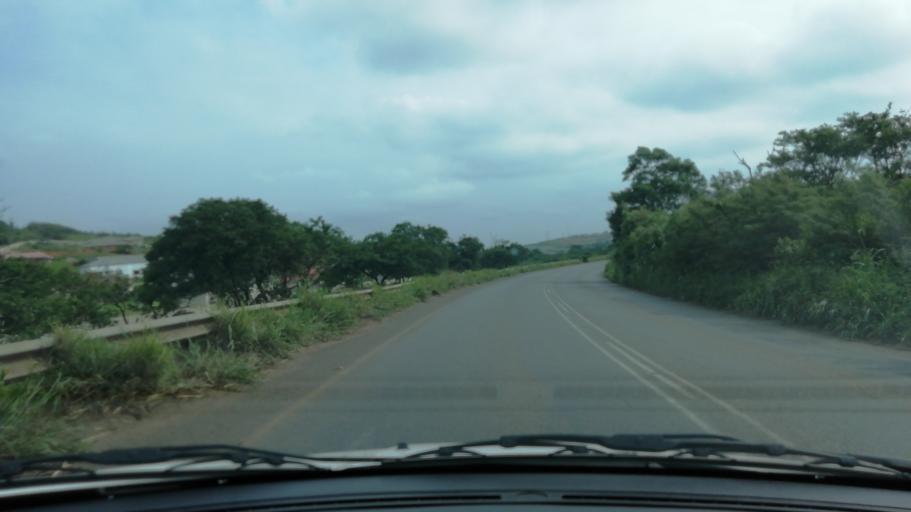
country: ZA
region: KwaZulu-Natal
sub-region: uThungulu District Municipality
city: Empangeni
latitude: -28.7480
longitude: 31.8804
